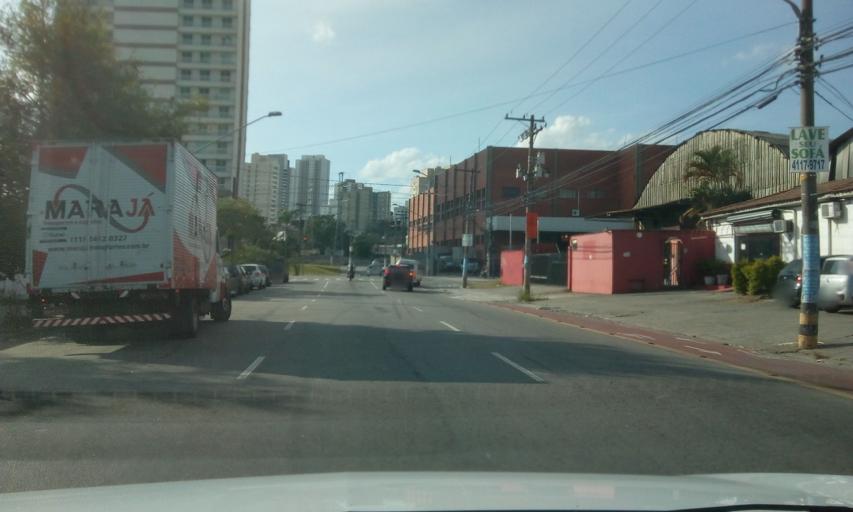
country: BR
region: Sao Paulo
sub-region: Sao Paulo
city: Sao Paulo
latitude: -23.5055
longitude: -46.6801
